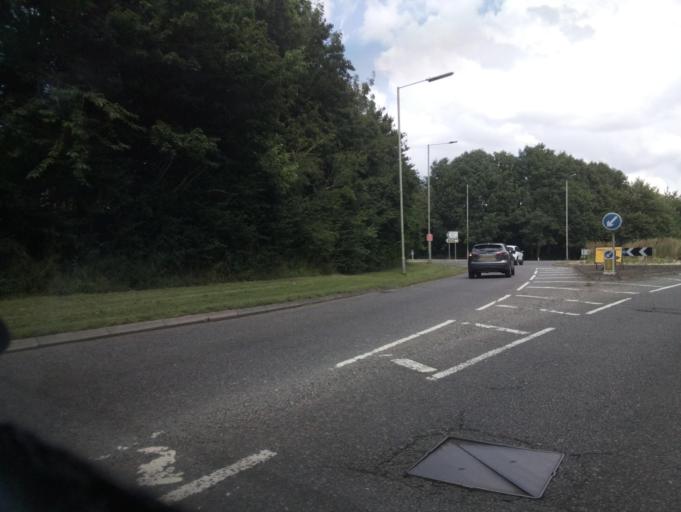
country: GB
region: England
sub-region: Wiltshire
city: Purton
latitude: 51.5801
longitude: -1.8323
